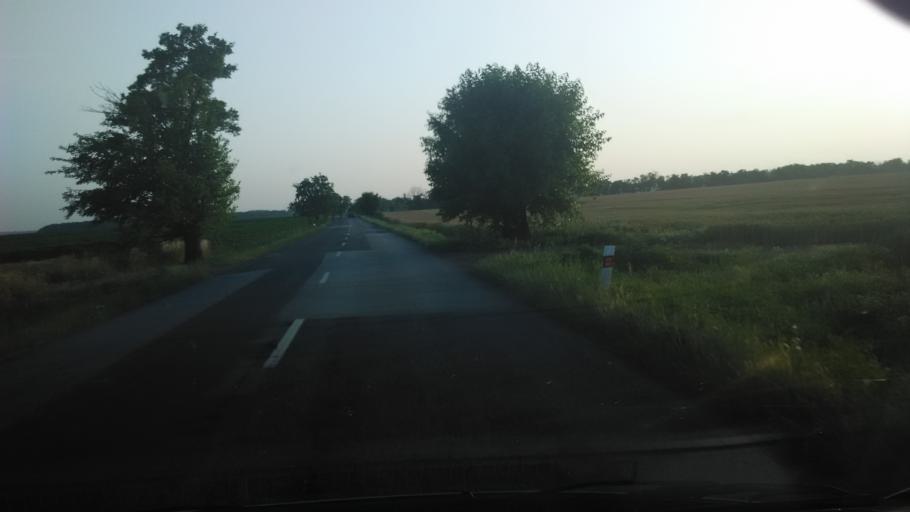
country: SK
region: Nitriansky
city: Tlmace
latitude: 48.1897
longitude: 18.4983
